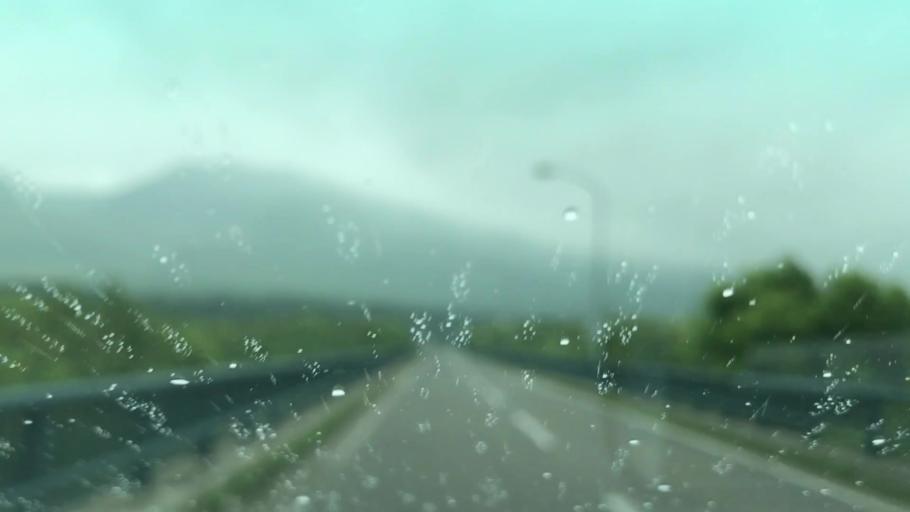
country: JP
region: Hokkaido
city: Iwanai
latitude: 42.7388
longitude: 140.2978
